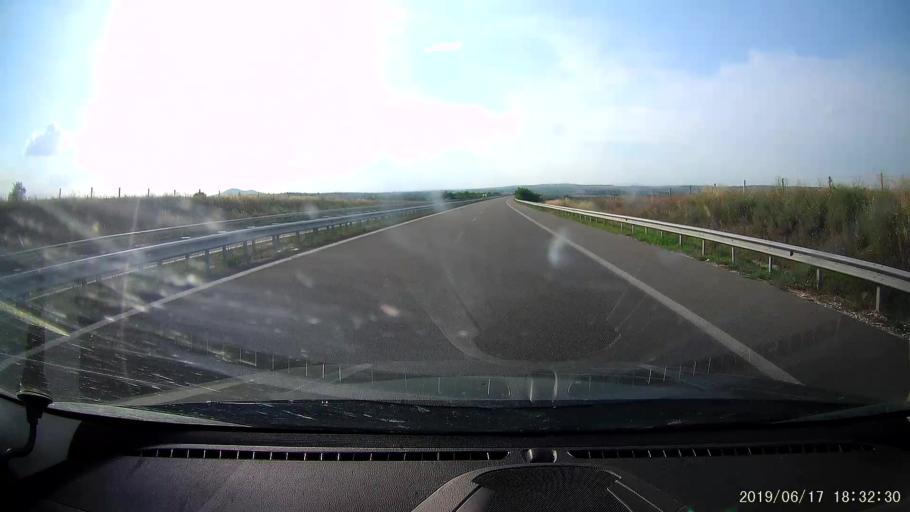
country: BG
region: Khaskovo
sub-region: Obshtina Dimitrovgrad
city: Dimitrovgrad
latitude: 42.0608
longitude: 25.4774
